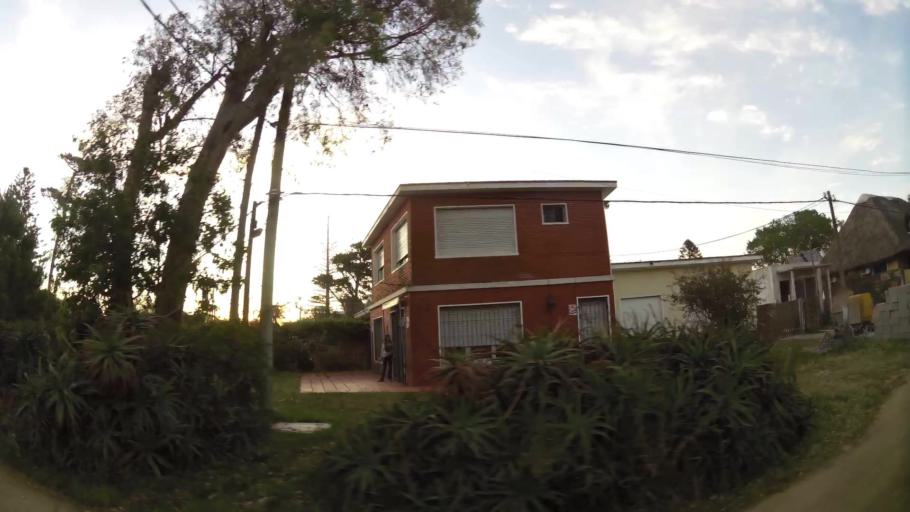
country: UY
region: Canelones
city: Atlantida
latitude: -34.7777
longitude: -55.7492
